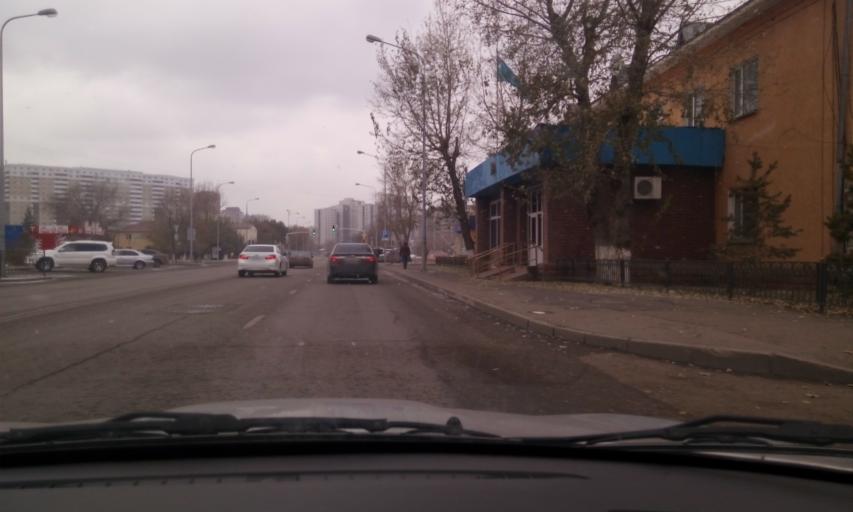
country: KZ
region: Astana Qalasy
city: Astana
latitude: 51.1632
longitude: 71.4518
